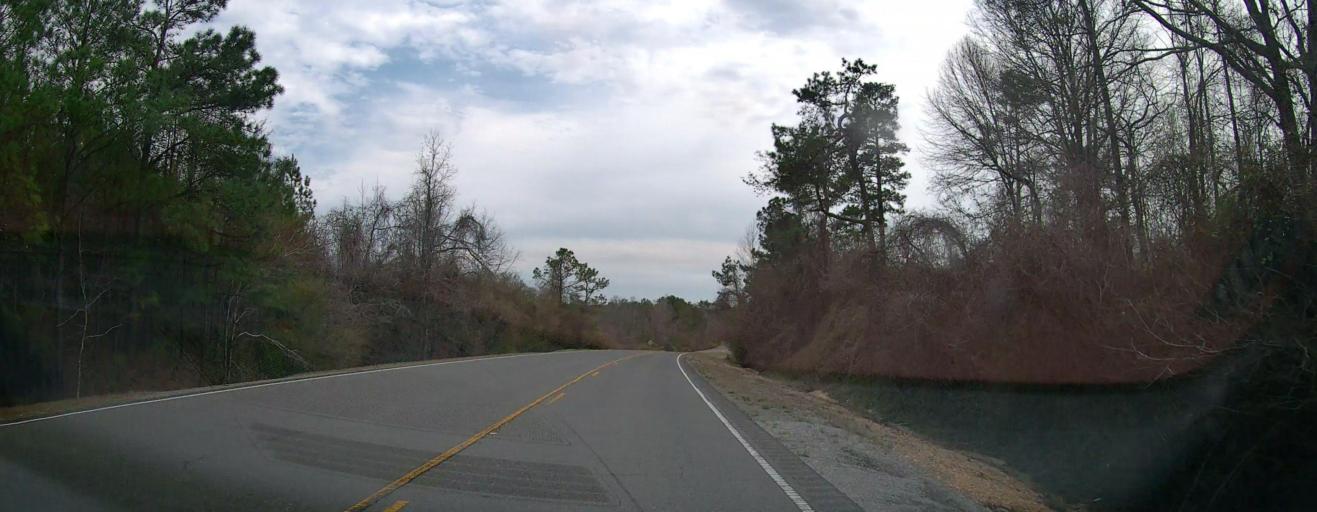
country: US
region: Alabama
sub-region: Marion County
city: Guin
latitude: 34.0279
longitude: -87.9415
